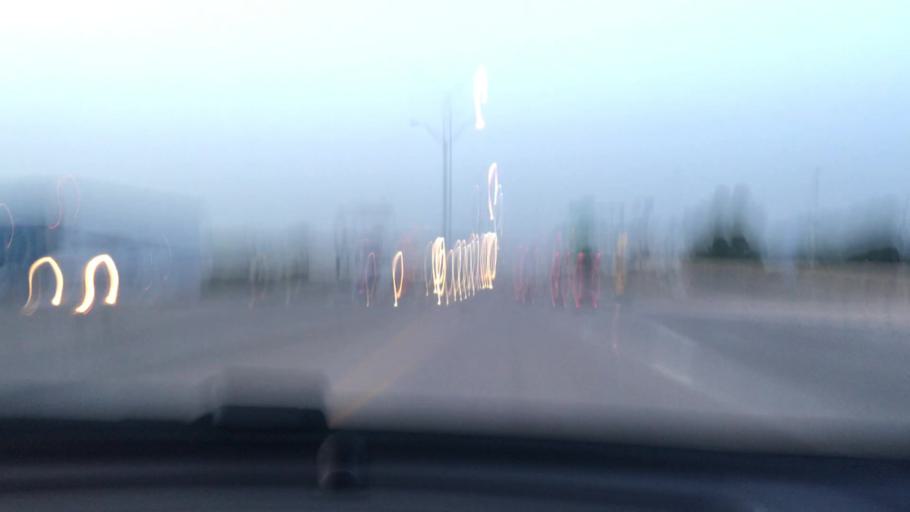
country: US
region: Texas
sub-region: Dallas County
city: DeSoto
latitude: 32.5899
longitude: -96.8225
